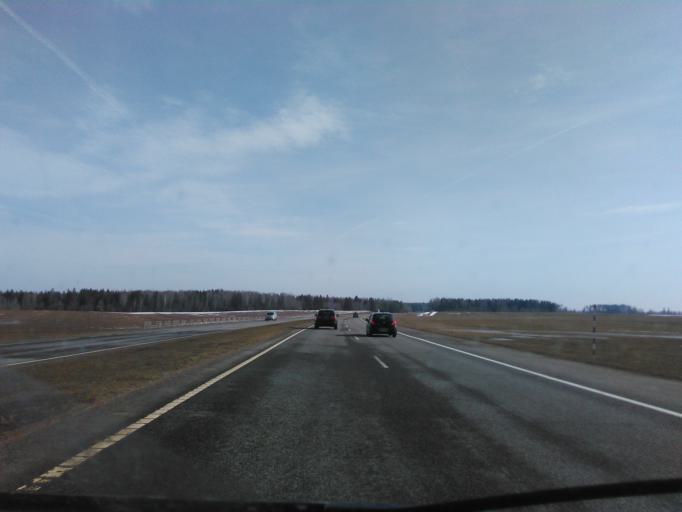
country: BY
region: Vitebsk
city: Talachyn
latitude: 54.4794
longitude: 29.8290
